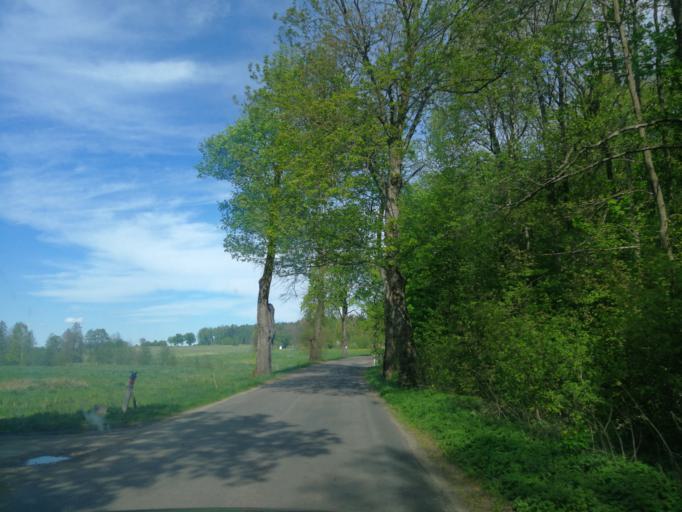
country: PL
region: Warmian-Masurian Voivodeship
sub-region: Powiat ilawski
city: Ilawa
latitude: 53.6684
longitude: 19.6566
